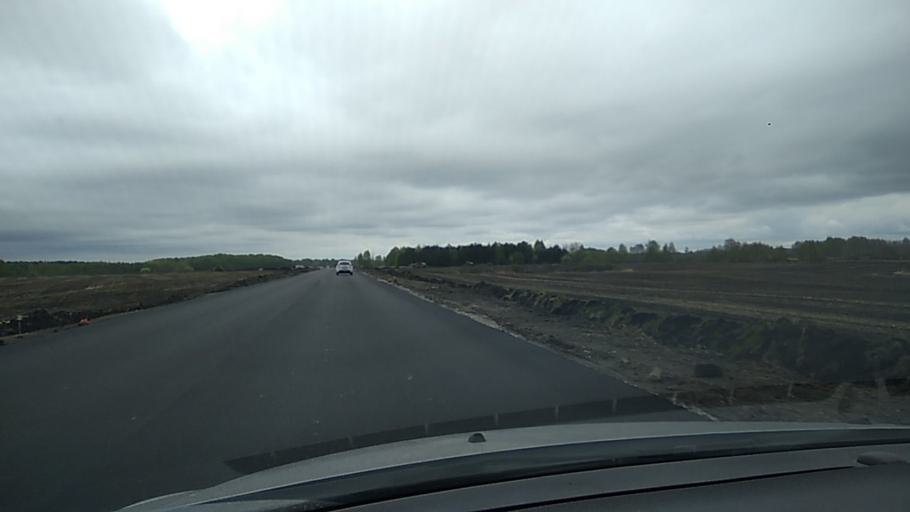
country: RU
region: Kurgan
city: Shadrinsk
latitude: 56.1546
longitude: 63.4007
